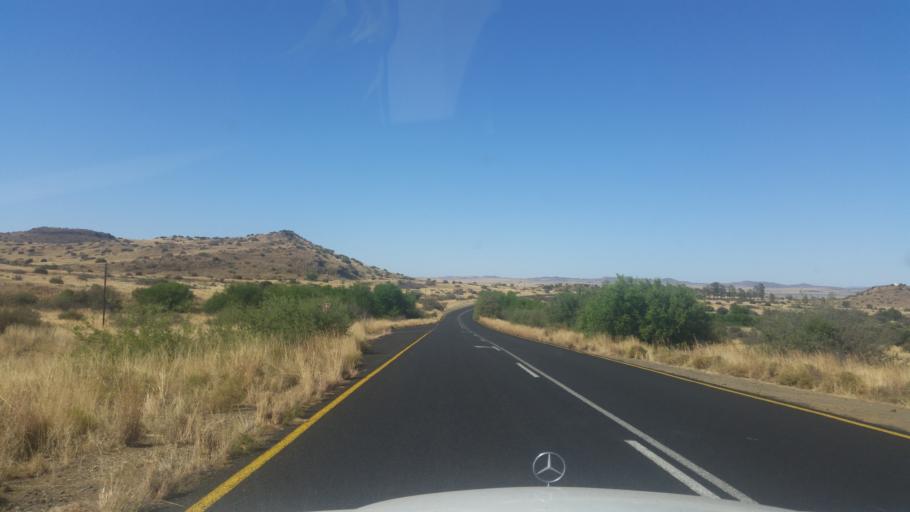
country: ZA
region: Orange Free State
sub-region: Xhariep District Municipality
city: Trompsburg
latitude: -30.4779
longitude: 25.9997
